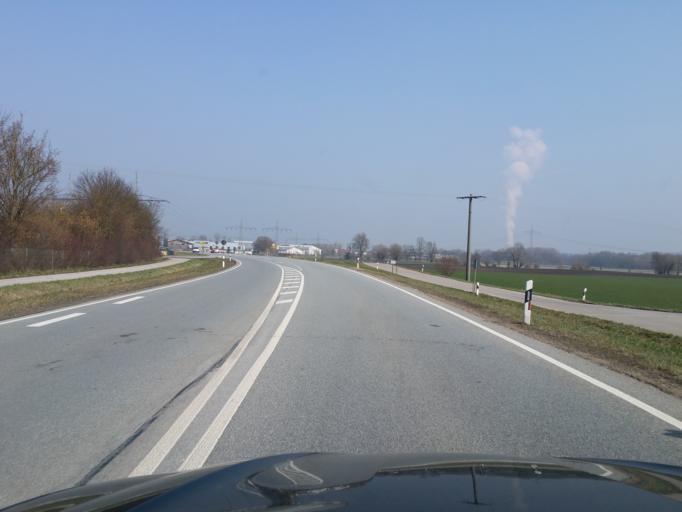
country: DE
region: Bavaria
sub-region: Lower Bavaria
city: Ergolding
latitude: 48.5794
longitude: 12.1938
